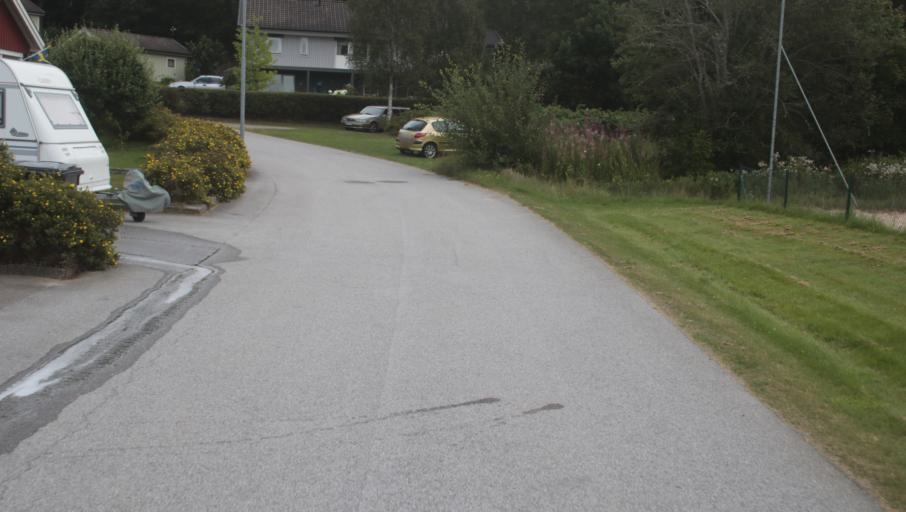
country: SE
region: Blekinge
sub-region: Karlshamns Kommun
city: Karlshamn
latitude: 56.1996
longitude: 14.9471
